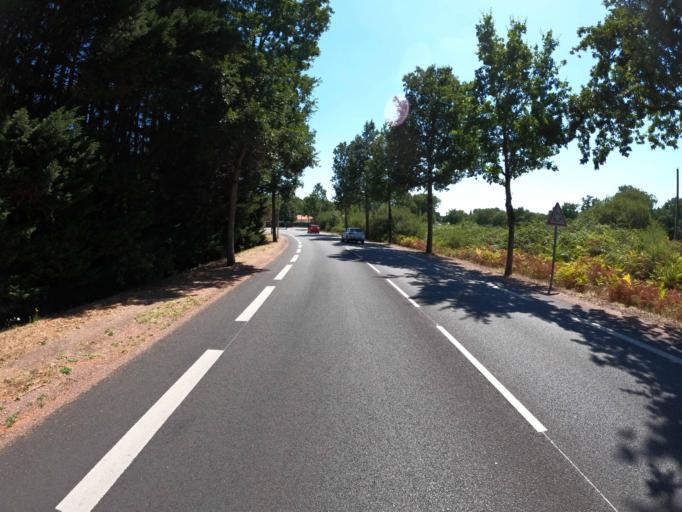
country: FR
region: Pays de la Loire
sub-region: Departement de la Vendee
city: Challans
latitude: 46.8402
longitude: -1.8942
